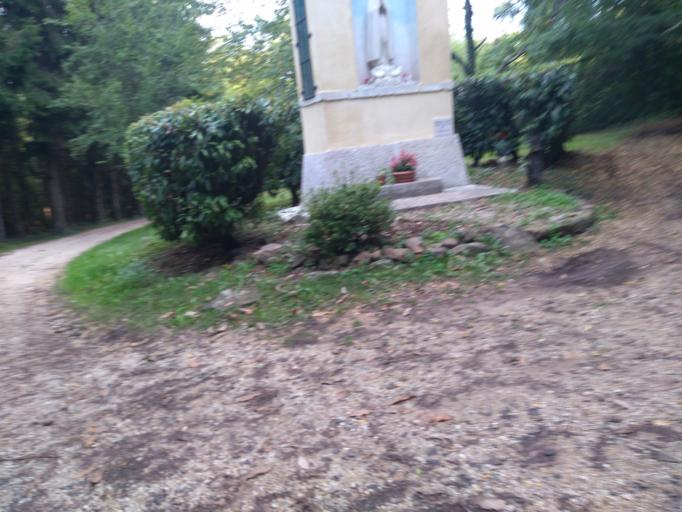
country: IT
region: Veneto
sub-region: Provincia di Vicenza
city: Monte di Malo
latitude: 45.6683
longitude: 11.3501
